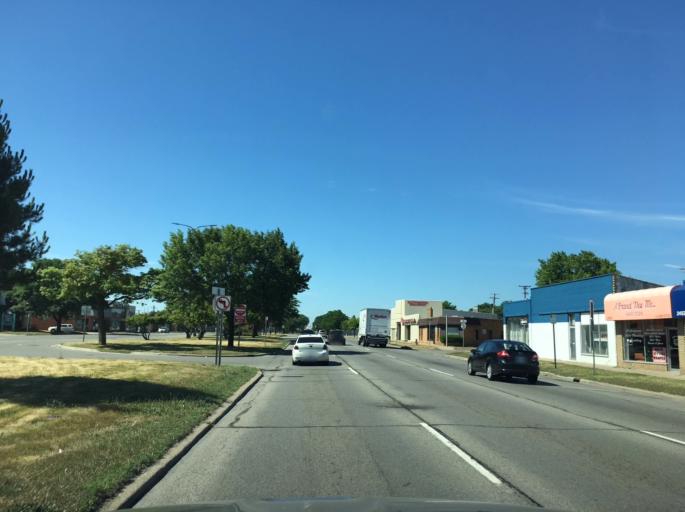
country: US
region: Michigan
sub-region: Macomb County
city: Eastpointe
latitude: 42.4757
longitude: -82.9509
